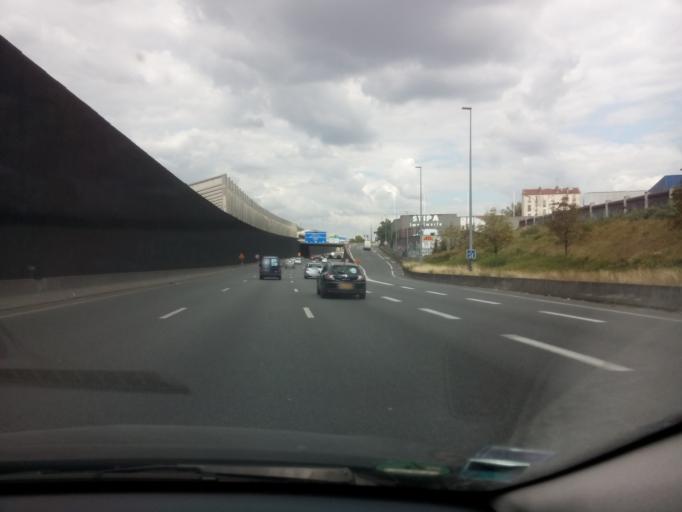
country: FR
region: Ile-de-France
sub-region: Departement de Seine-Saint-Denis
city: Bagnolet
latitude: 48.8691
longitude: 2.4294
